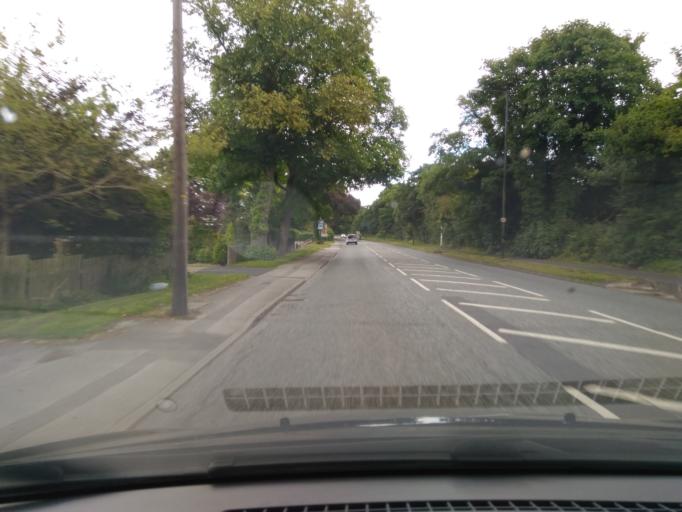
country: GB
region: England
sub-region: North Yorkshire
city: Knaresborough
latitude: 54.0051
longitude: -1.4891
